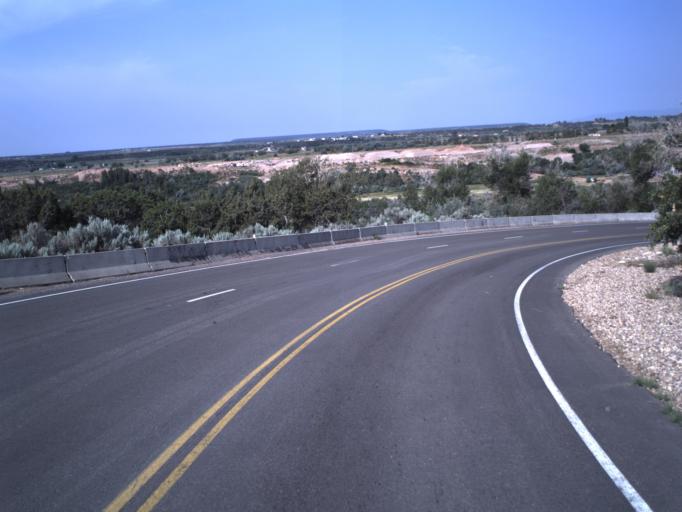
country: US
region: Utah
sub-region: Duchesne County
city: Duchesne
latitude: 40.3551
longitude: -110.3097
